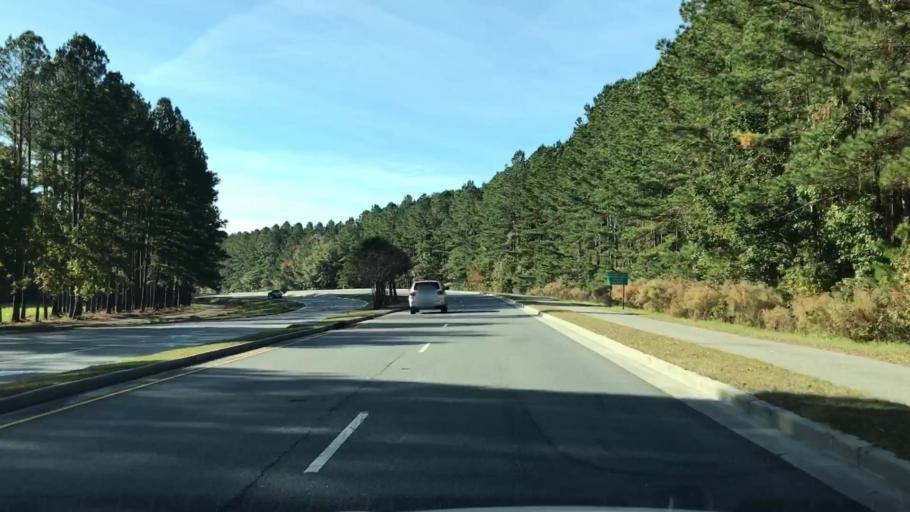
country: US
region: South Carolina
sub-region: Beaufort County
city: Bluffton
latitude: 32.2802
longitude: -80.9127
